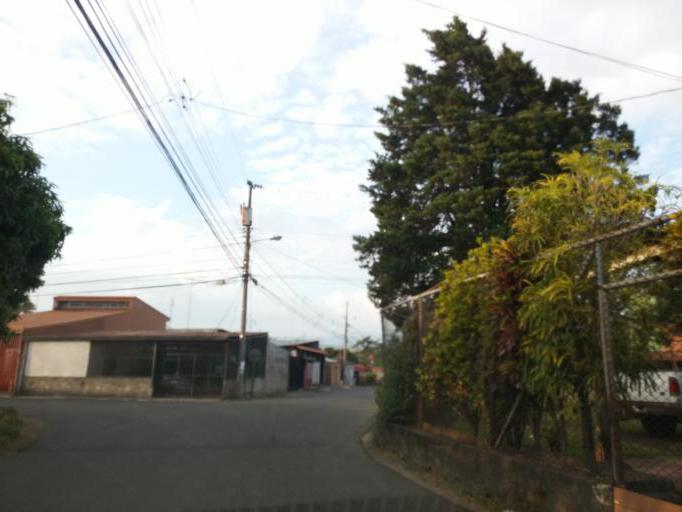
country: CR
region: Alajuela
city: Alajuela
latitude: 10.0017
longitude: -84.2203
